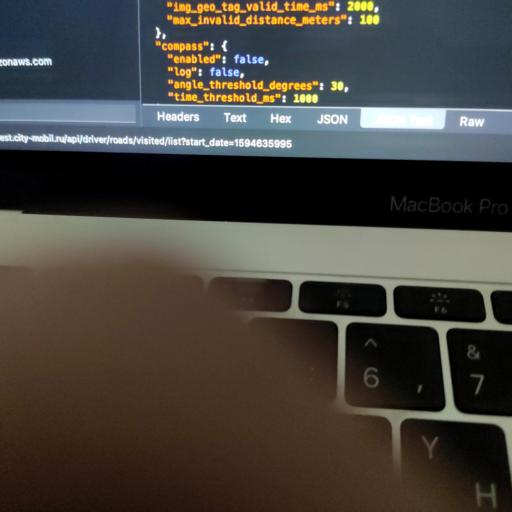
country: RU
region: Krasnodarskiy
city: Kudepsta
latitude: 43.4946
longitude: 39.8881
